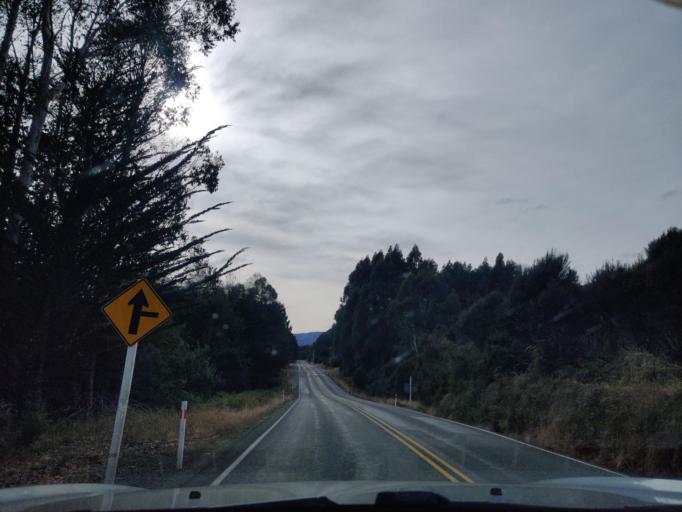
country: NZ
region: Tasman
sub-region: Tasman District
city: Wakefield
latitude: -41.7775
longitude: 172.9164
